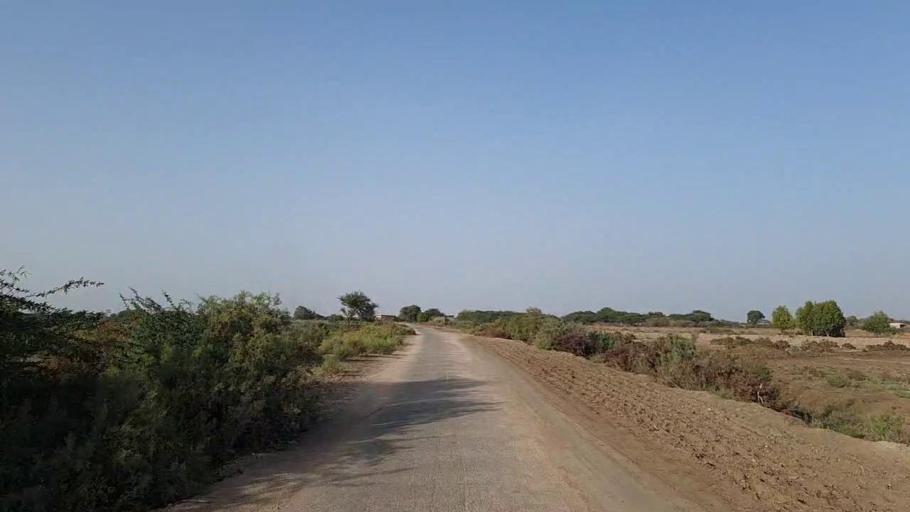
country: PK
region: Sindh
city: Jati
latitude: 24.3107
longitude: 68.1681
